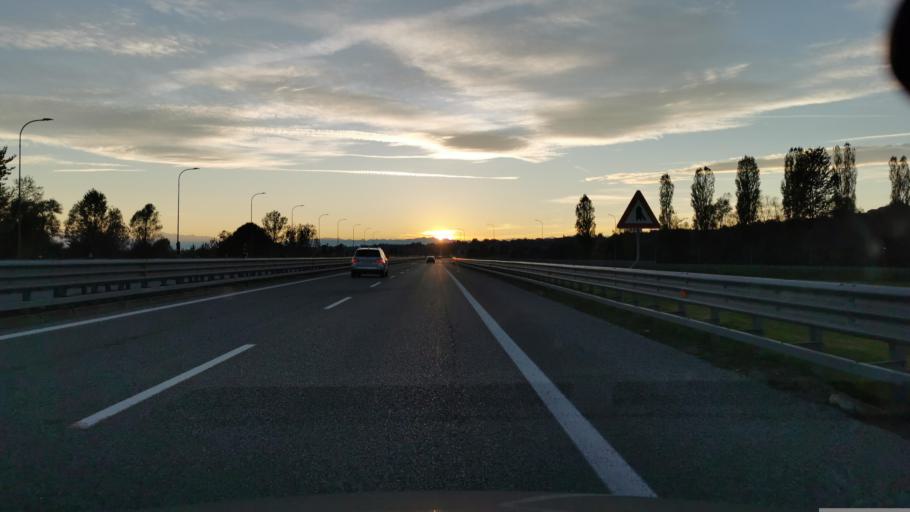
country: IT
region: Piedmont
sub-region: Provincia di Cuneo
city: Roreto
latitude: 44.6601
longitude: 7.8424
